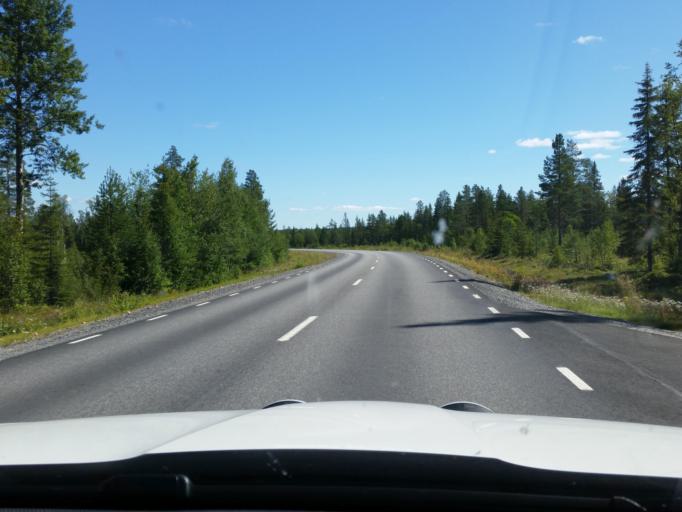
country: SE
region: Vaesterbotten
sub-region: Skelleftea Kommun
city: Storvik
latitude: 65.3241
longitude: 20.7687
